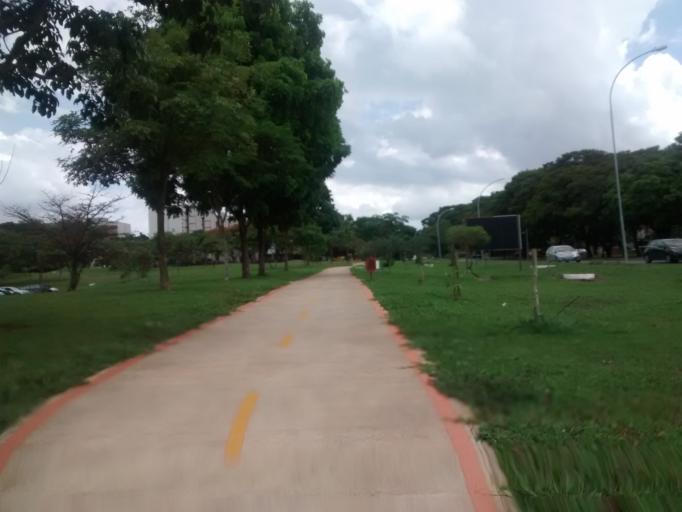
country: BR
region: Federal District
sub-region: Brasilia
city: Brasilia
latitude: -15.7668
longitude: -47.8861
